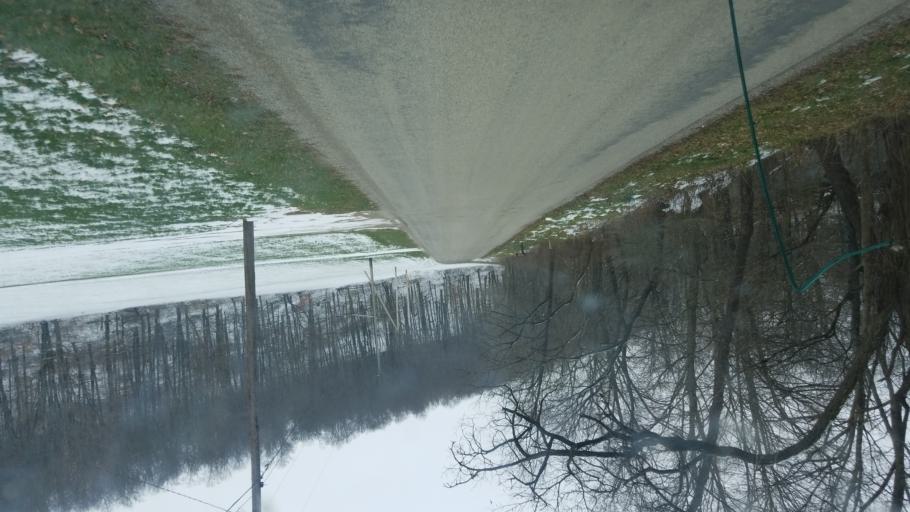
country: US
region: Ohio
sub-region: Sandusky County
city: Bellville
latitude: 40.6132
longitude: -82.5025
